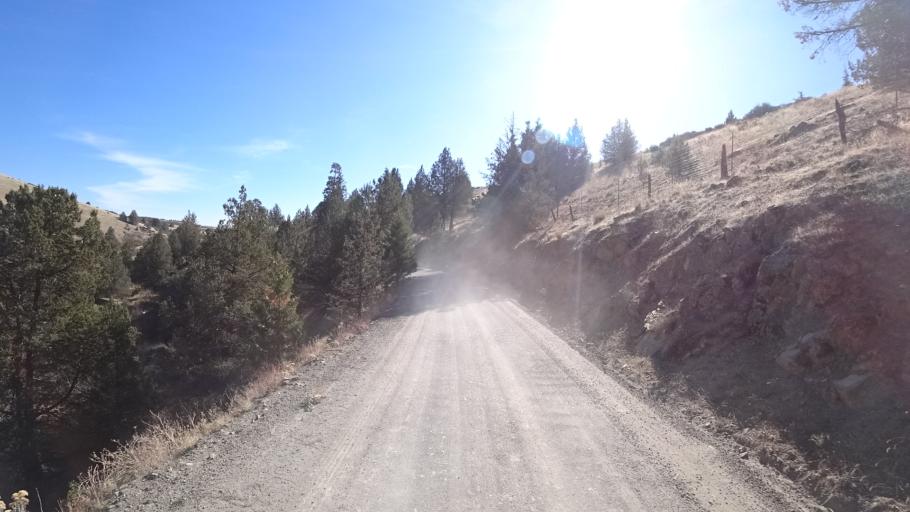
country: US
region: California
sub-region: Siskiyou County
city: Yreka
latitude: 41.7815
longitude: -122.5985
